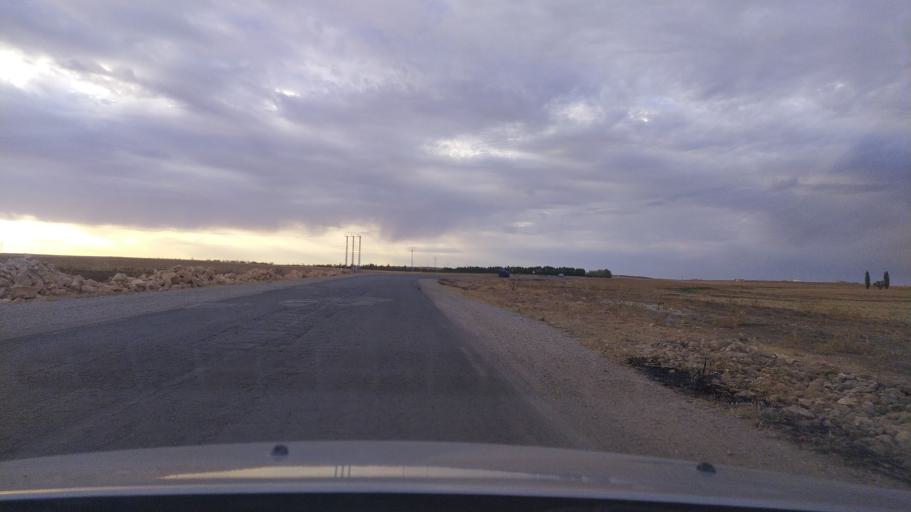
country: DZ
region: Tiaret
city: Frenda
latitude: 34.9815
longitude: 1.1462
